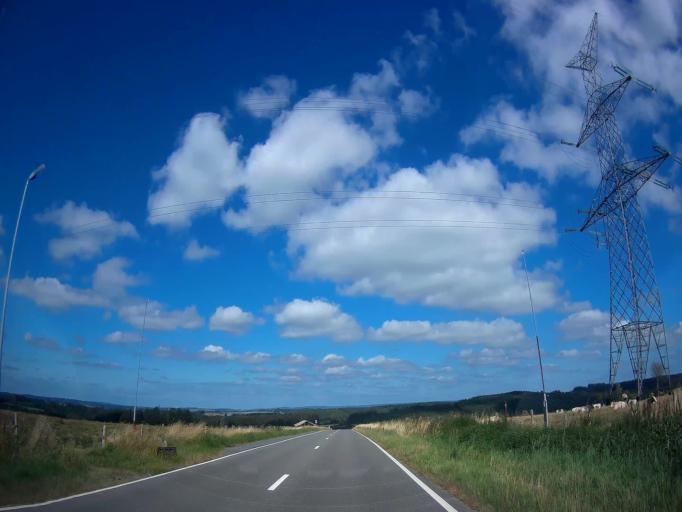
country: BE
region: Wallonia
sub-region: Province du Luxembourg
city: Bastogne
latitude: 50.0233
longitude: 5.7051
